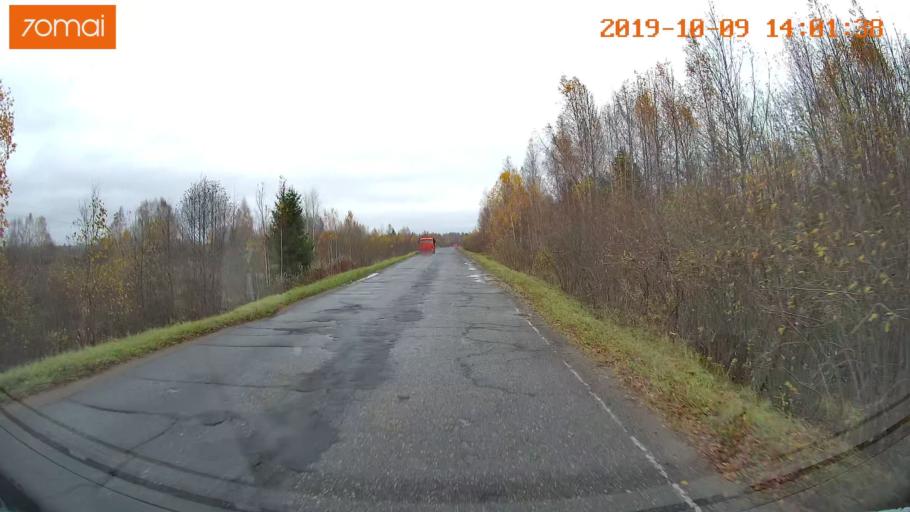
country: RU
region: Kostroma
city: Buy
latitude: 58.4447
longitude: 41.3491
